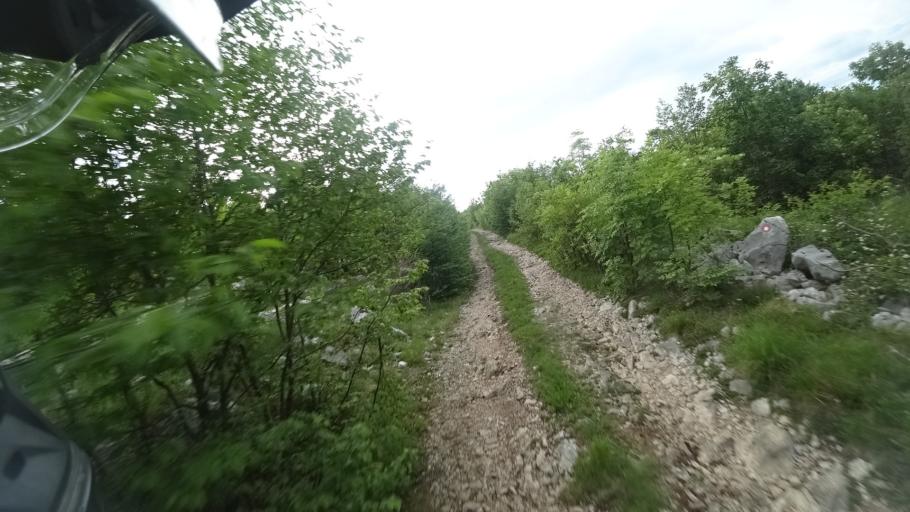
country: HR
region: Sibensko-Kniniska
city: Drnis
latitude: 43.8709
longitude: 16.3812
